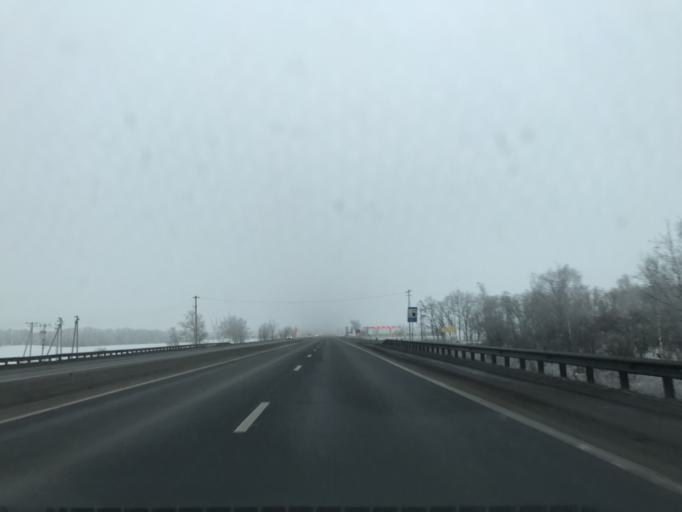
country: RU
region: Rostov
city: Grushevskaya
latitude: 47.4615
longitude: 39.9733
